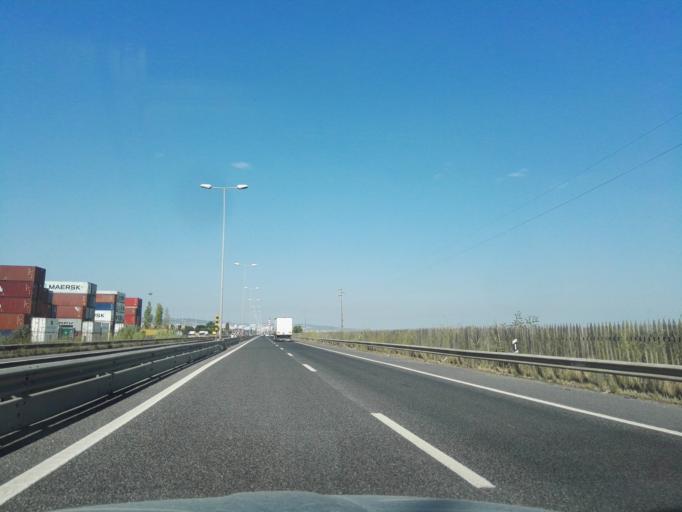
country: PT
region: Lisbon
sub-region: Loures
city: Bobadela
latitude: 38.8065
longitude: -9.0908
